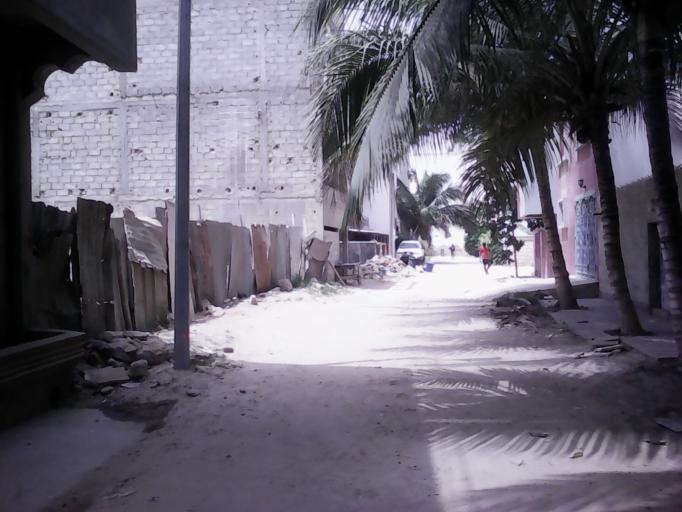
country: SN
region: Dakar
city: Grand Dakar
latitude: 14.7325
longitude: -17.4298
